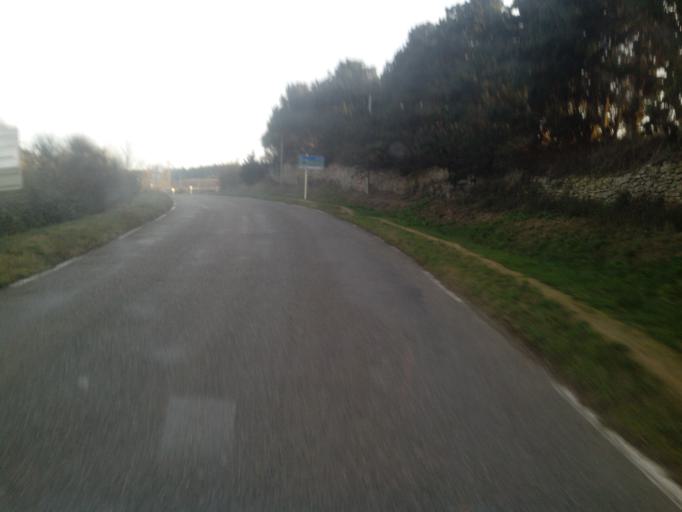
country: FR
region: Languedoc-Roussillon
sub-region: Departement de l'Aude
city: Cazilhac
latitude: 43.2044
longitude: 2.3721
